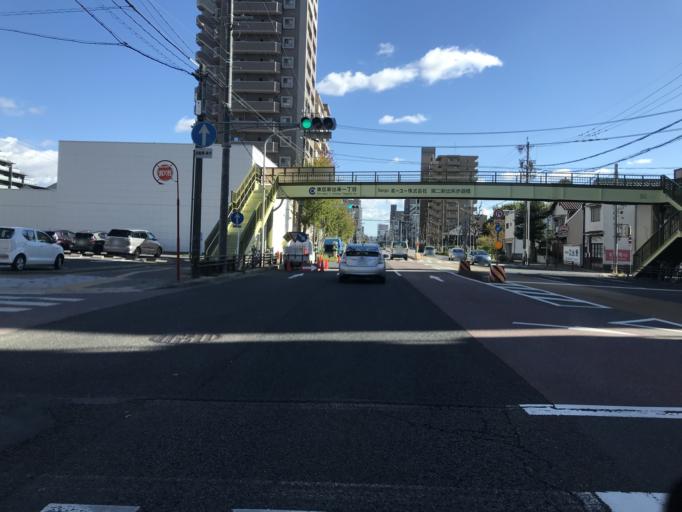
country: JP
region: Aichi
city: Nagoya-shi
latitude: 35.1828
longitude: 136.9288
